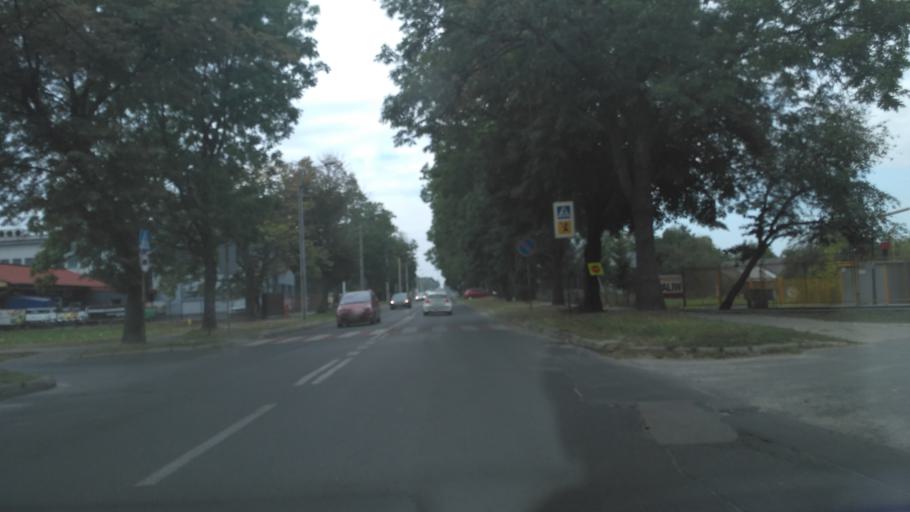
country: PL
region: Lublin Voivodeship
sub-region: Chelm
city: Chelm
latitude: 51.1443
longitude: 23.4427
